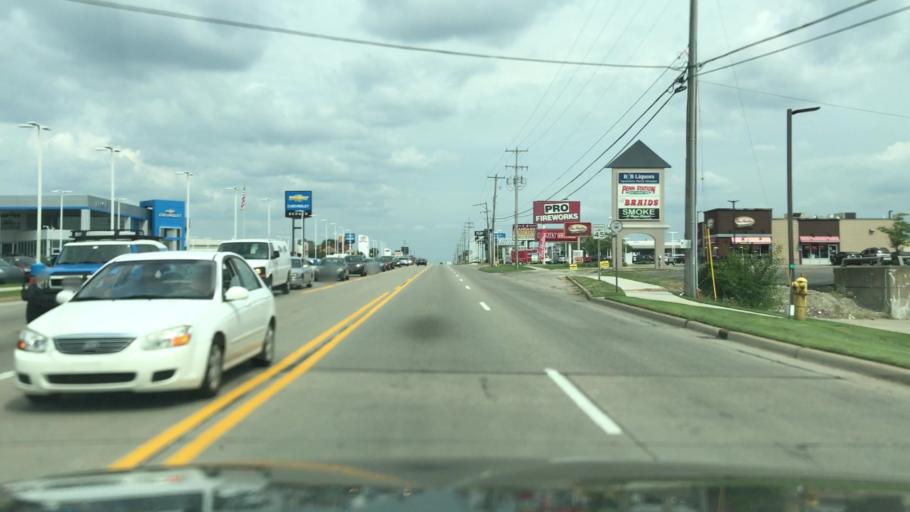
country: US
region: Michigan
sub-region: Kent County
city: East Grand Rapids
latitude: 42.9126
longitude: -85.6071
